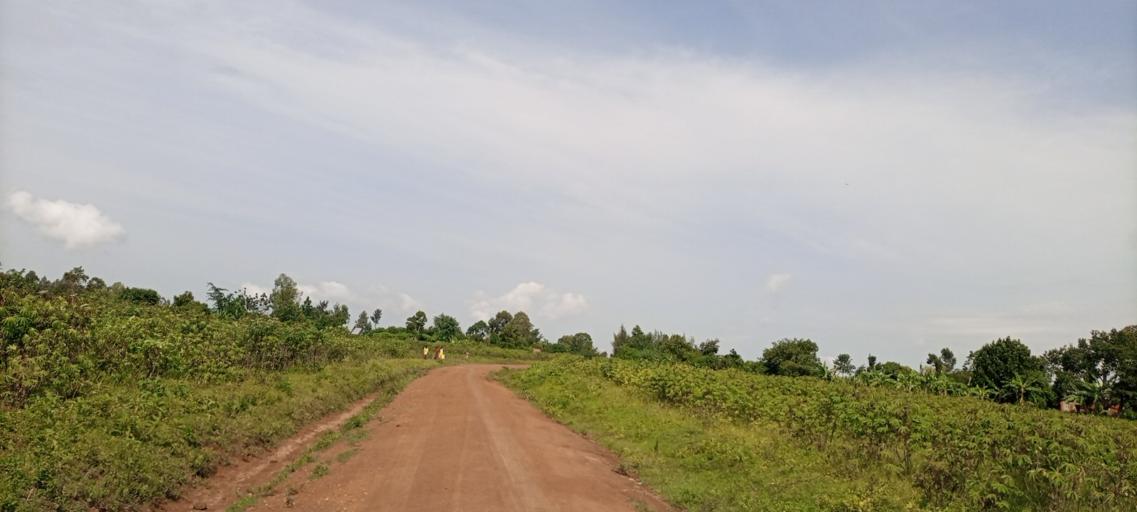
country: UG
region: Eastern Region
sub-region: Mbale District
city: Mbale
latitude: 1.1359
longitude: 34.0574
